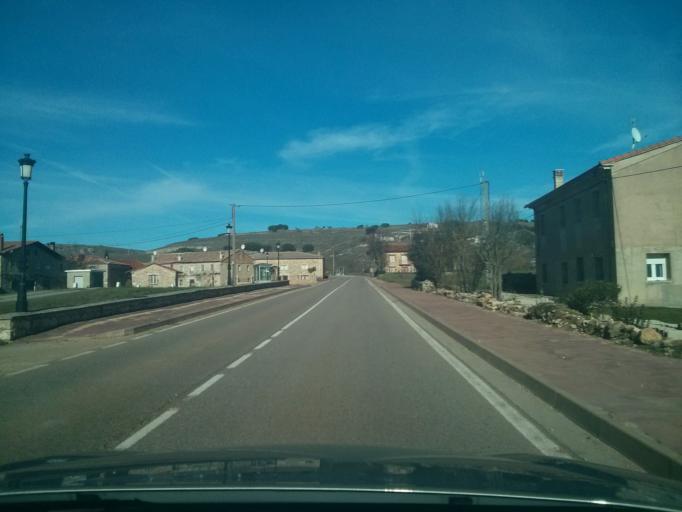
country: ES
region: Castille and Leon
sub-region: Provincia de Burgos
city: Abajas
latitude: 42.6378
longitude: -3.6233
